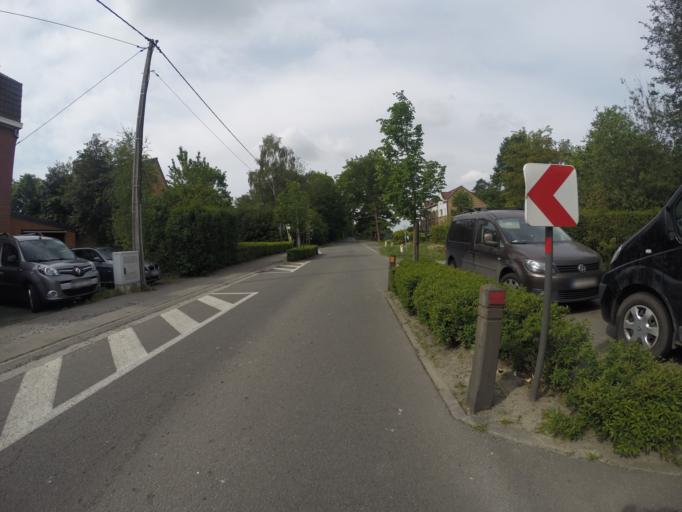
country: BE
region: Flanders
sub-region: Provincie West-Vlaanderen
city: Beernem
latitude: 51.0790
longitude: 3.3447
